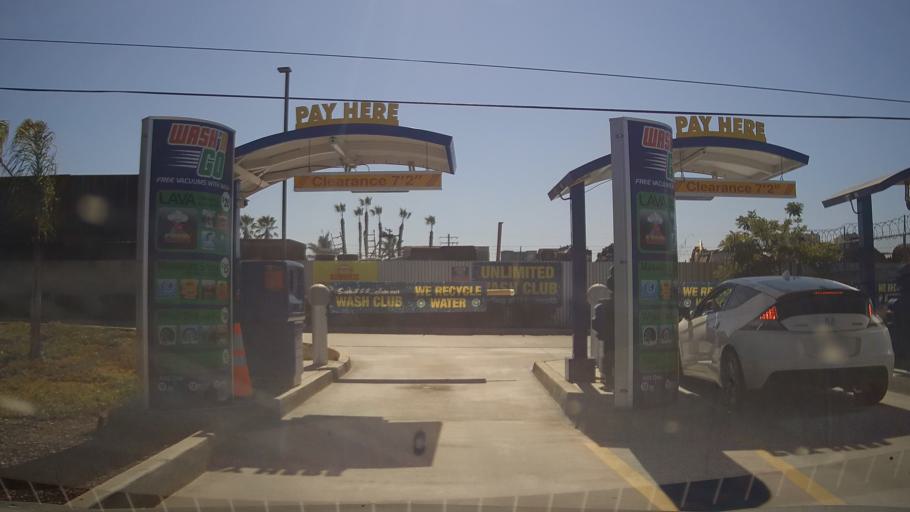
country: US
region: California
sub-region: San Diego County
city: San Diego
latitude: 32.8211
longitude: -117.1520
